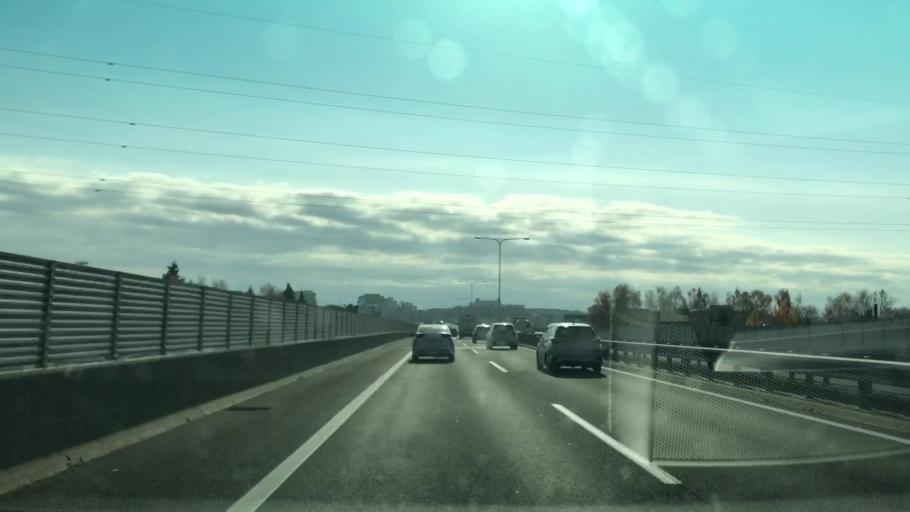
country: JP
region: Hokkaido
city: Sapporo
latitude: 43.0371
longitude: 141.4409
